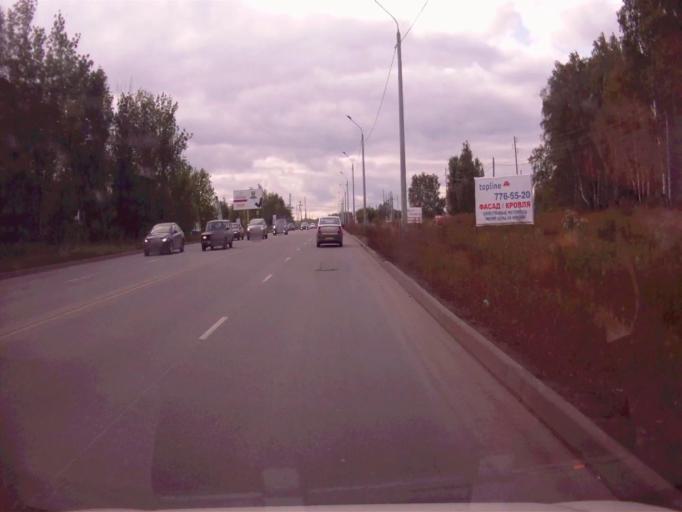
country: RU
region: Chelyabinsk
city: Sargazy
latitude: 55.1462
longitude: 61.2926
